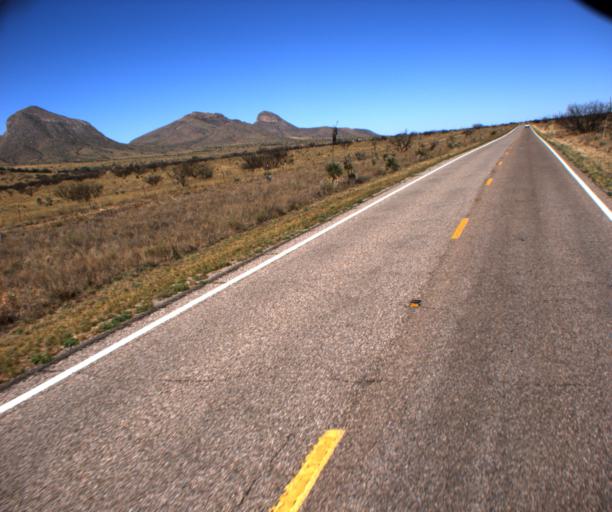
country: US
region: Arizona
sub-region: Cochise County
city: Huachuca City
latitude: 31.7020
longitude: -110.4324
